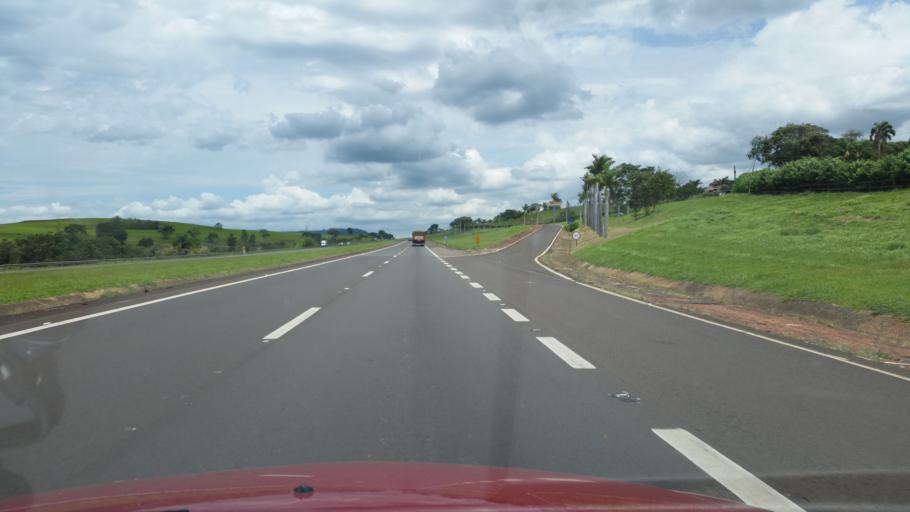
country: BR
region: Sao Paulo
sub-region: Itatinga
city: Itatinga
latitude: -23.1413
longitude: -48.4279
